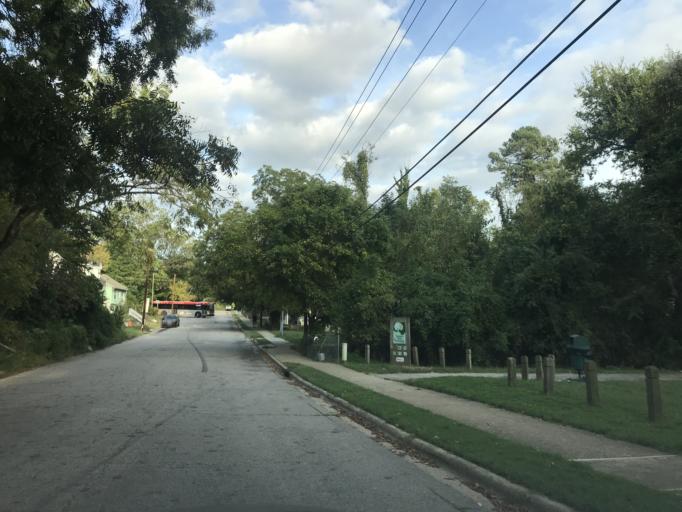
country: US
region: North Carolina
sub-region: Wake County
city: Raleigh
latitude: 35.7657
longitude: -78.6296
